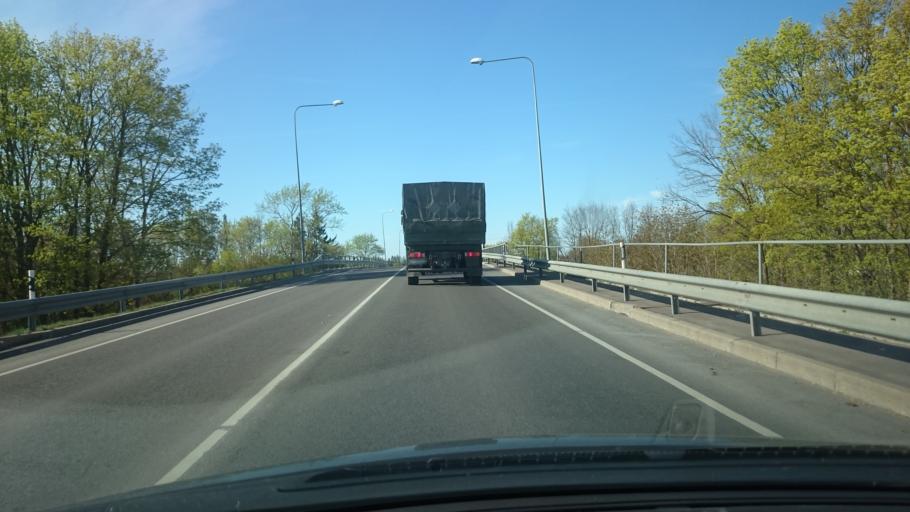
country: EE
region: Laeaene-Virumaa
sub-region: Rakvere linn
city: Rakvere
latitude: 59.3539
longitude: 26.3372
